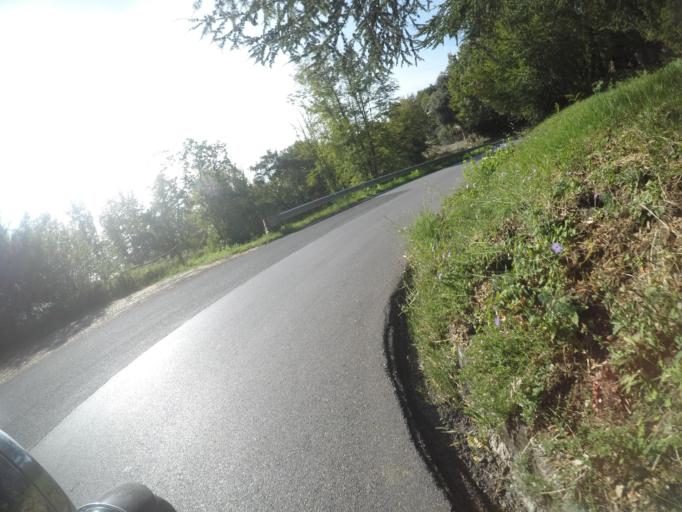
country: IT
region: Tuscany
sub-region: Provincia di Massa-Carrara
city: Massa
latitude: 44.0639
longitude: 10.1232
